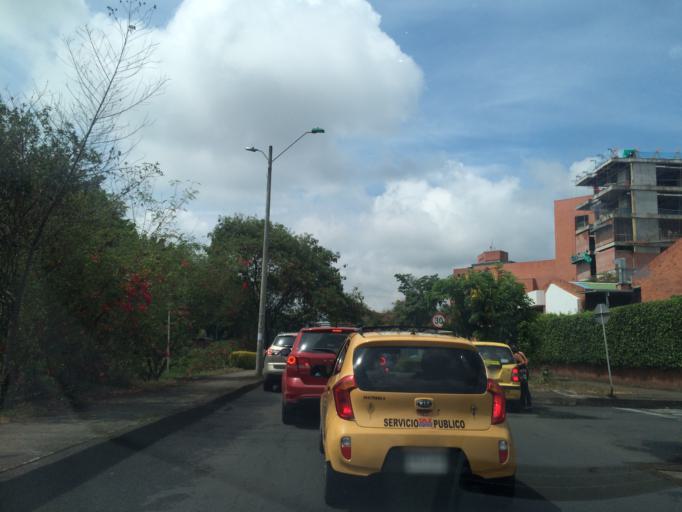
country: CO
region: Valle del Cauca
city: Cali
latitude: 3.3749
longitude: -76.5254
